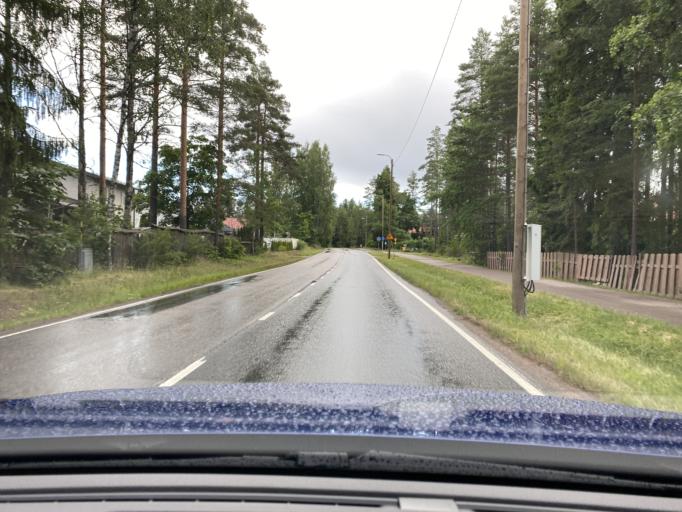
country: FI
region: Uusimaa
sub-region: Helsinki
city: Nurmijaervi
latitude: 60.5701
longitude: 24.7626
